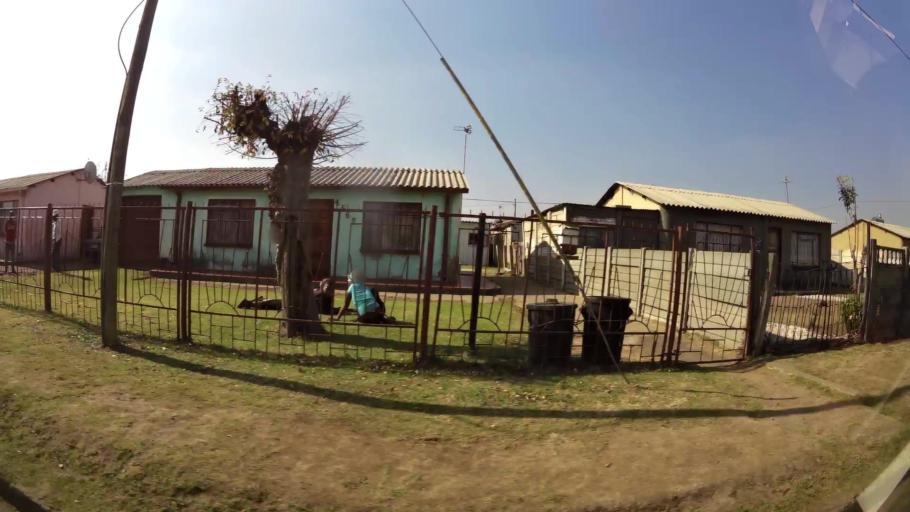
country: ZA
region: Gauteng
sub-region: Ekurhuleni Metropolitan Municipality
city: Brakpan
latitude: -26.1409
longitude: 28.4203
